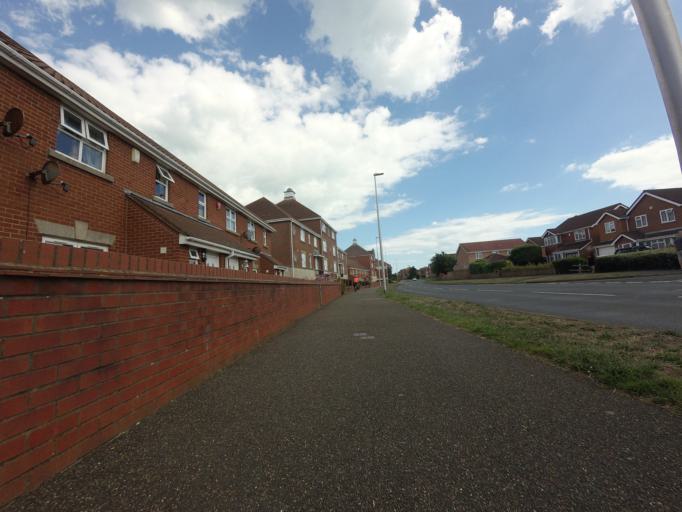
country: GB
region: England
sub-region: East Sussex
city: Pevensey
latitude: 50.7887
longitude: 0.3241
